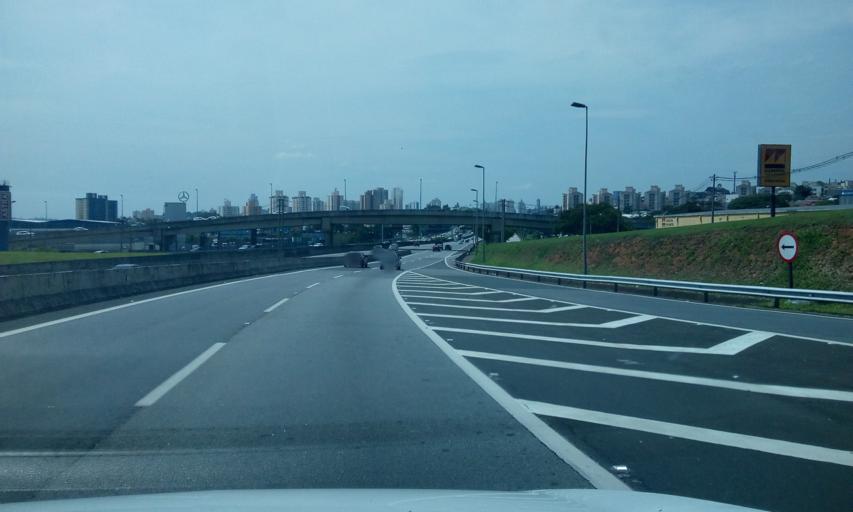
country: BR
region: Sao Paulo
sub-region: Jundiai
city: Jundiai
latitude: -23.1727
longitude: -46.9224
